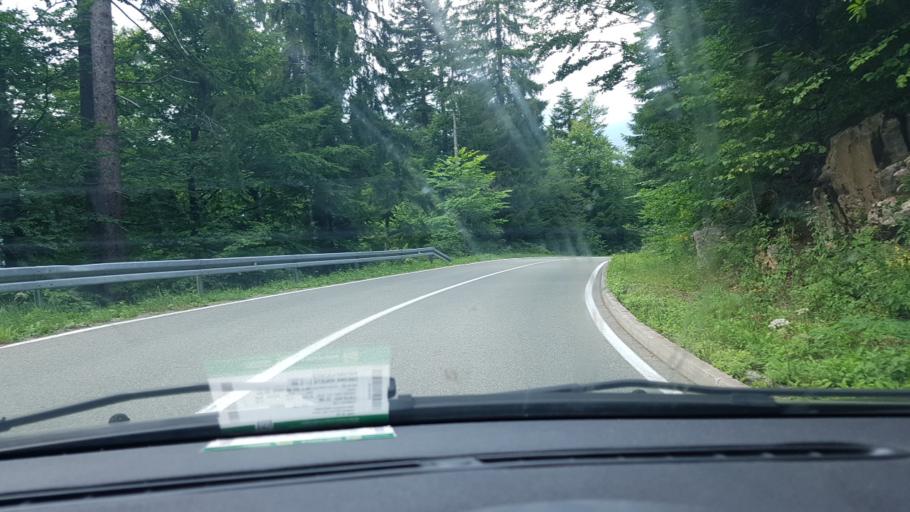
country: HR
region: Primorsko-Goranska
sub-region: Grad Delnice
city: Delnice
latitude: 45.3443
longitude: 14.7580
